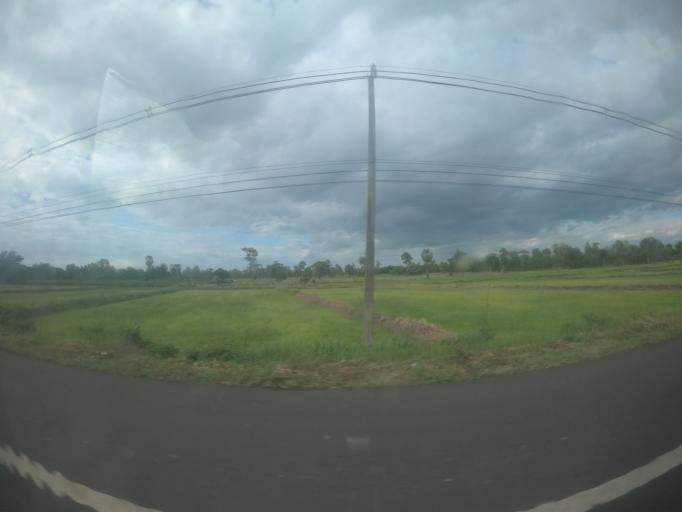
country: TH
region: Surin
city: Kap Choeng
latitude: 14.5350
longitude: 103.5264
